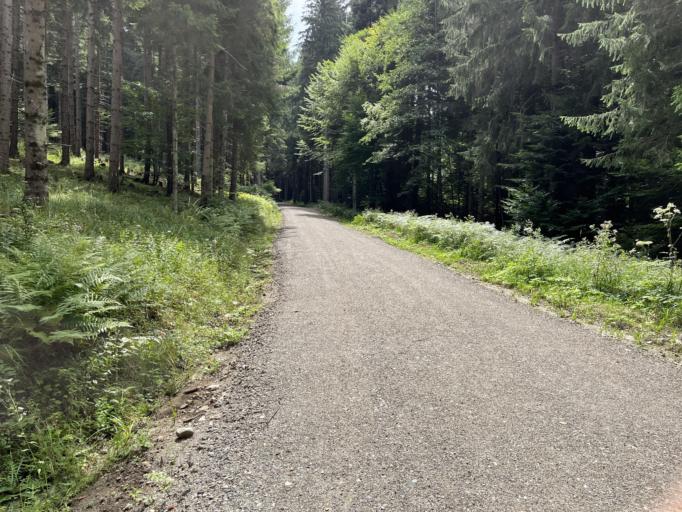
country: AT
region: Carinthia
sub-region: Politischer Bezirk Spittal an der Drau
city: Millstatt
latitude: 46.7954
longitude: 13.5467
